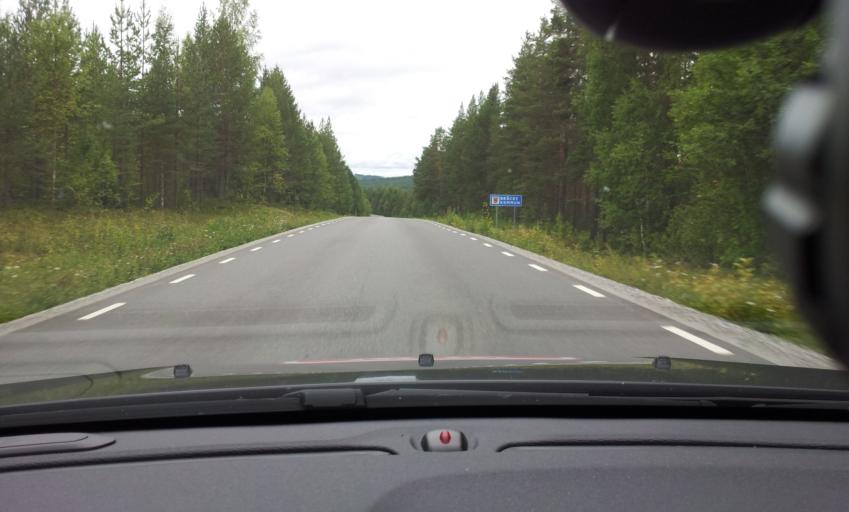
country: SE
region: Jaemtland
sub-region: Braecke Kommun
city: Braecke
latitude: 63.1039
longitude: 15.4528
